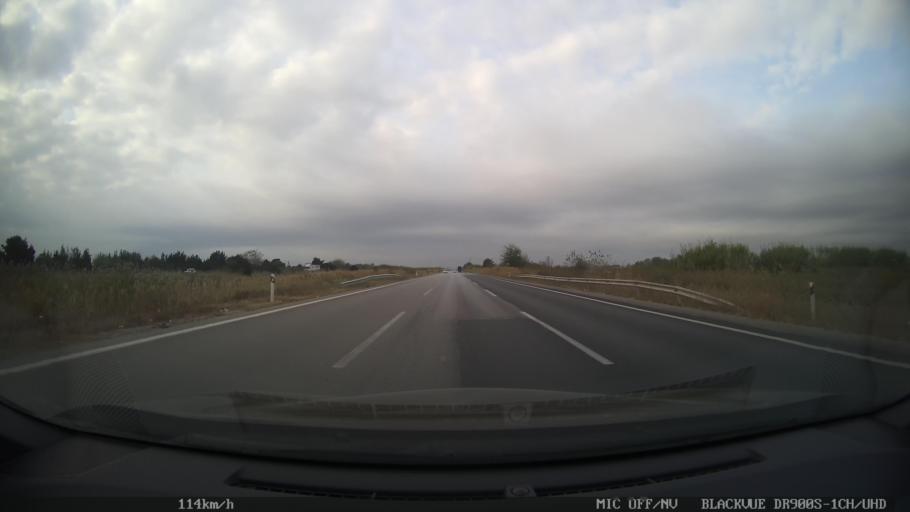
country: GR
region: Central Macedonia
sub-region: Nomos Thessalonikis
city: Chalastra
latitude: 40.6313
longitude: 22.7762
